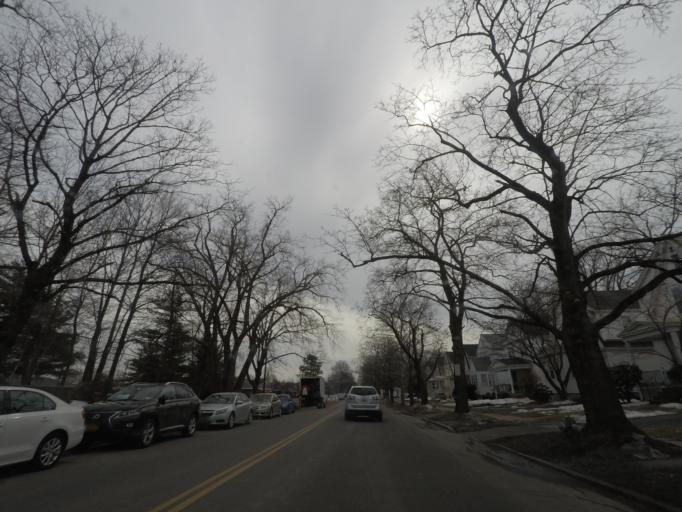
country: US
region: New York
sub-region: Albany County
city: Albany
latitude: 42.6494
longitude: -73.7854
